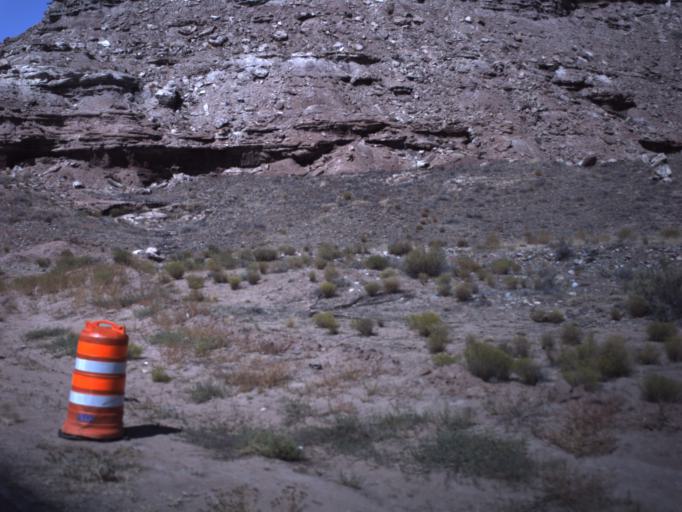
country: US
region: Utah
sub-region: San Juan County
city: Blanding
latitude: 37.2574
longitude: -109.2890
